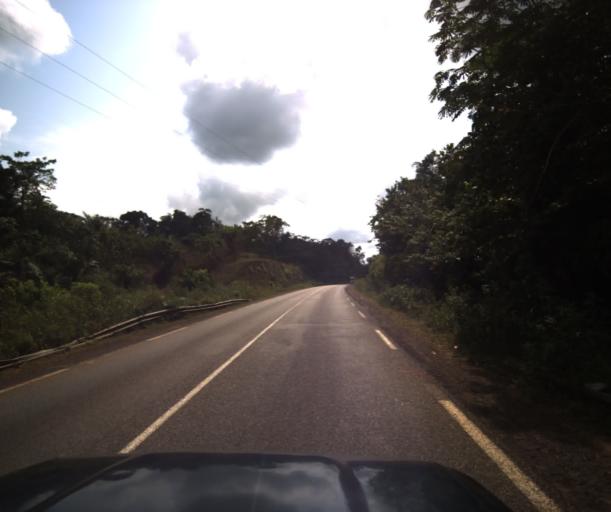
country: CM
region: Littoral
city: Edea
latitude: 3.8044
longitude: 10.2308
